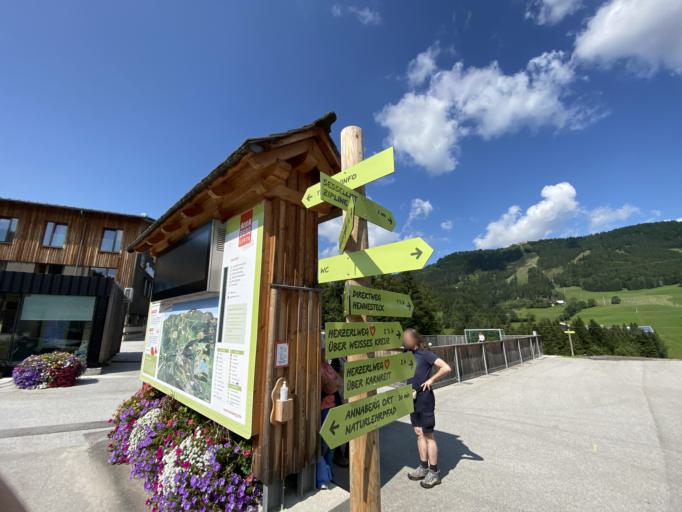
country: AT
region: Lower Austria
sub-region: Politischer Bezirk Lilienfeld
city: Annaberg
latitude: 47.8756
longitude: 15.3666
